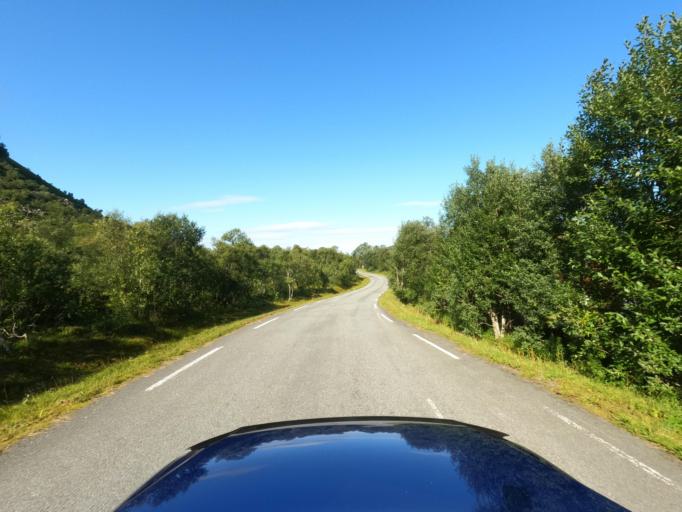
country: NO
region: Nordland
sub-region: Vagan
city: Kabelvag
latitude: 68.3173
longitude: 14.2421
